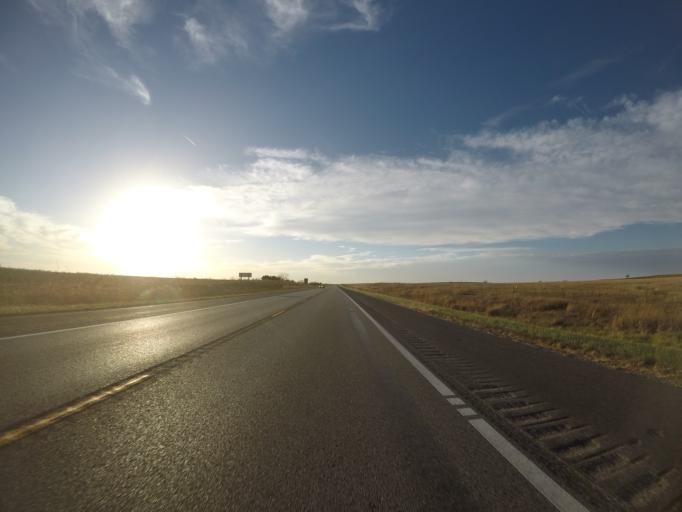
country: US
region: Kansas
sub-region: Chase County
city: Cottonwood Falls
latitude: 38.4056
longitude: -96.4293
